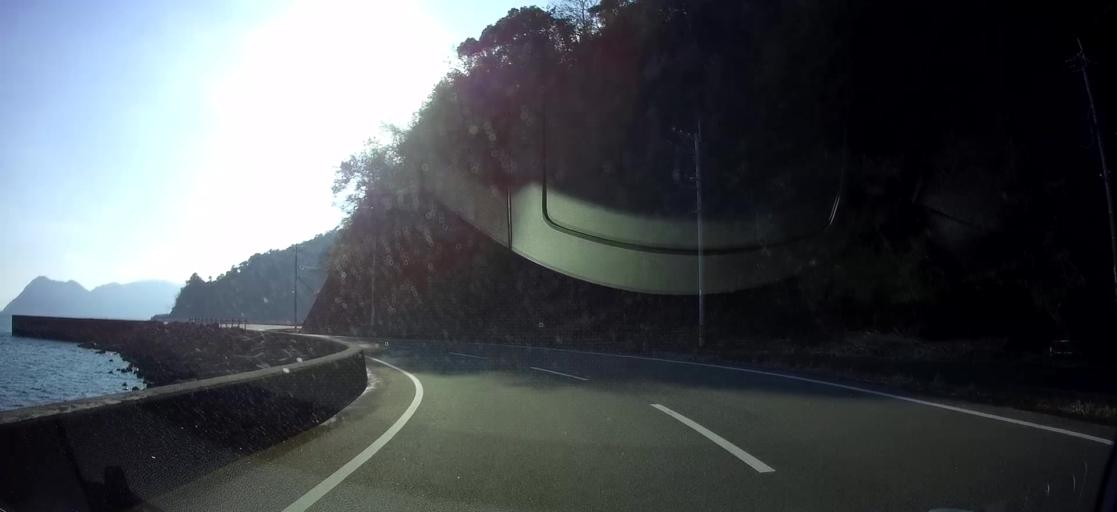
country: JP
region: Kumamoto
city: Minamata
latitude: 32.3885
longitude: 130.3851
